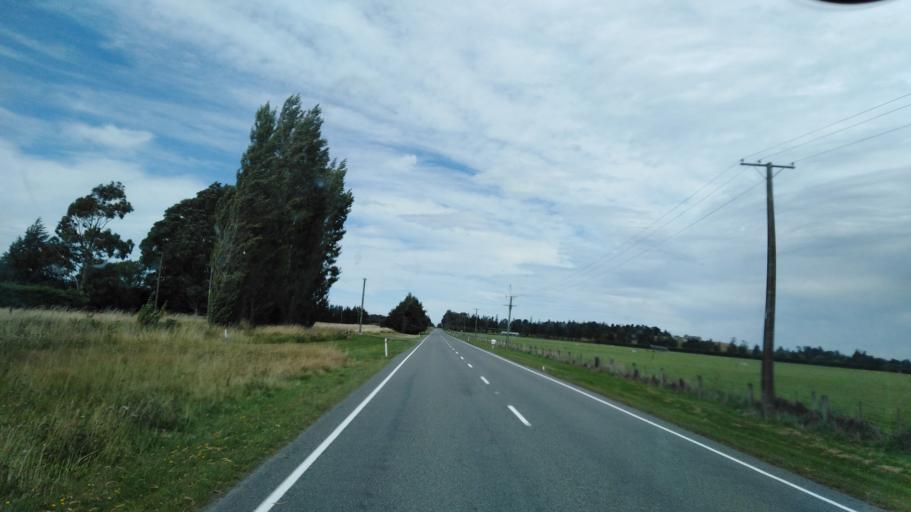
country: NZ
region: Canterbury
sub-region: Selwyn District
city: Darfield
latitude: -43.4324
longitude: 172.0596
